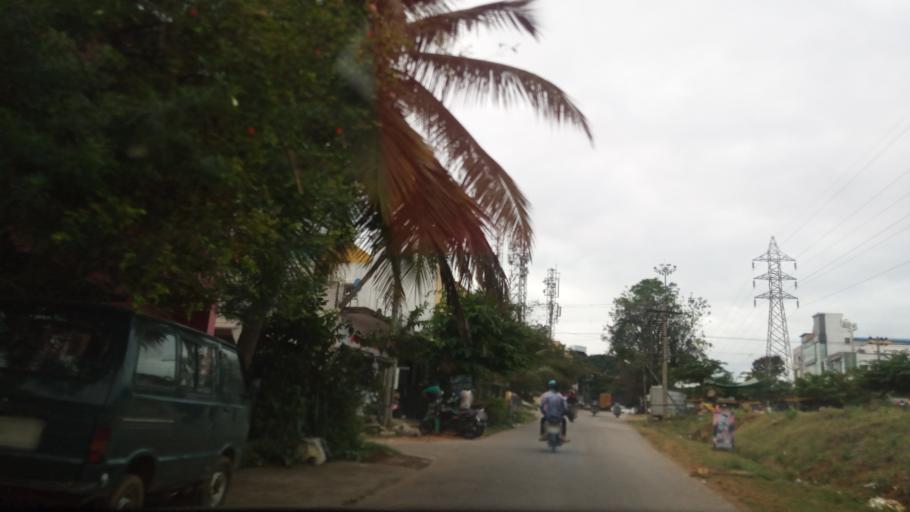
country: IN
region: Karnataka
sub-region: Mysore
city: Mysore
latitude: 12.2947
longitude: 76.6145
